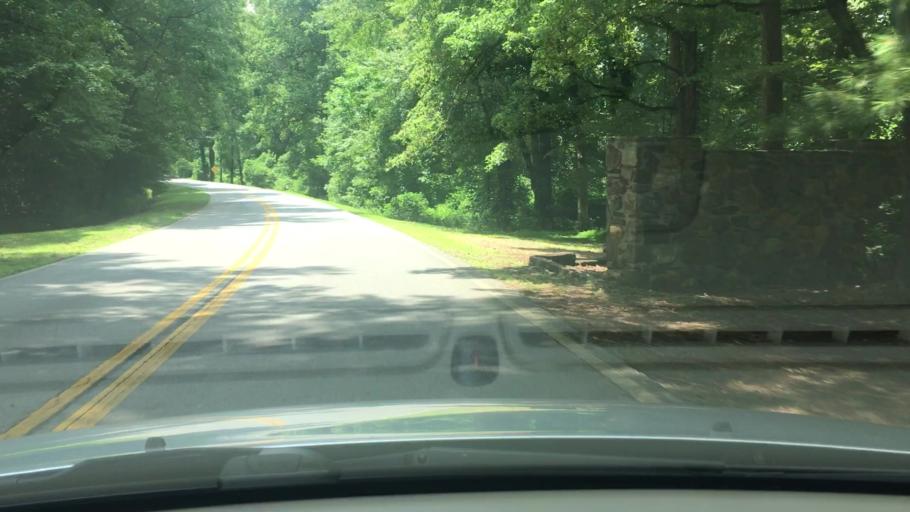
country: US
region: Georgia
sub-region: Dawson County
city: Dawsonville
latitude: 34.5572
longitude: -84.2504
